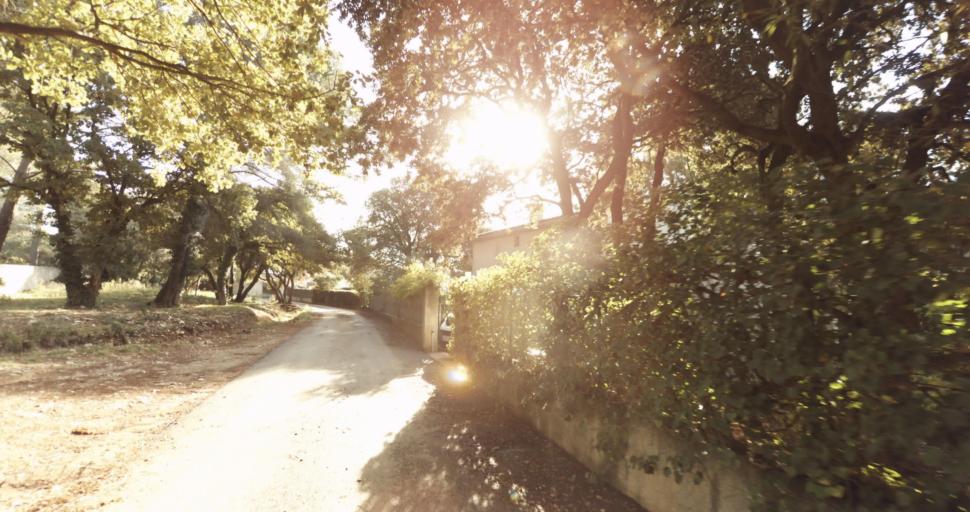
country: FR
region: Provence-Alpes-Cote d'Azur
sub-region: Departement des Bouches-du-Rhone
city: Venelles
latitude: 43.5926
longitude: 5.4654
